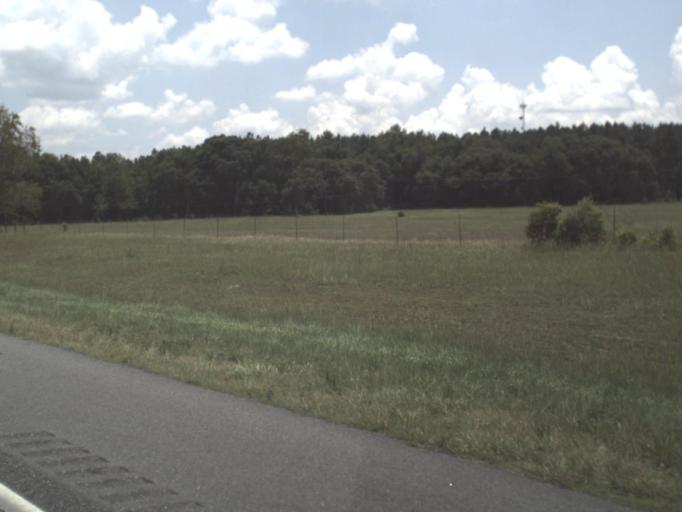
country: US
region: Florida
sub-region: Hamilton County
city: Jasper
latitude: 30.5111
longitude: -83.0507
